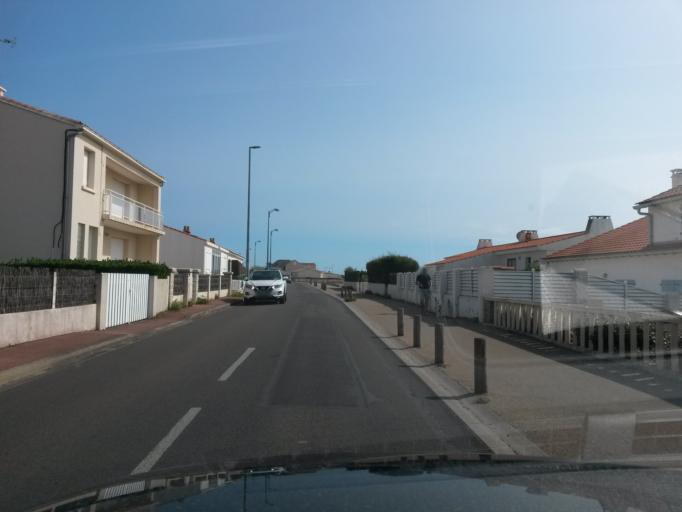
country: FR
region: Pays de la Loire
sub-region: Departement de la Vendee
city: Bretignolles-sur-Mer
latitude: 46.6239
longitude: -1.8735
